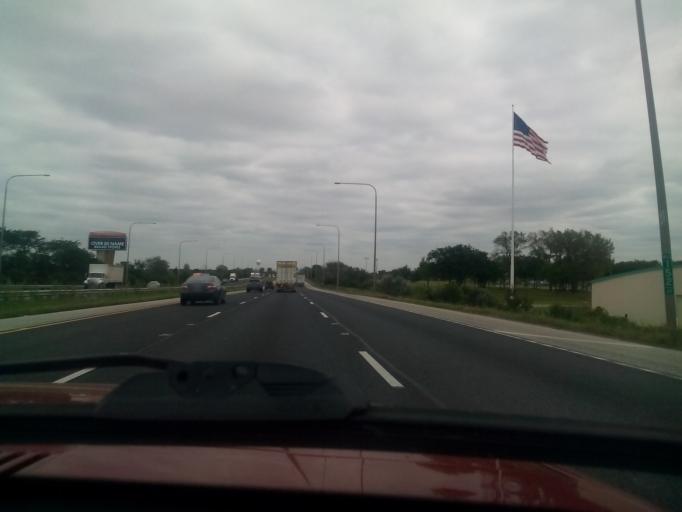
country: US
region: Illinois
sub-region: Cook County
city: Country Club Hills
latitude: 41.5727
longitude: -87.7278
